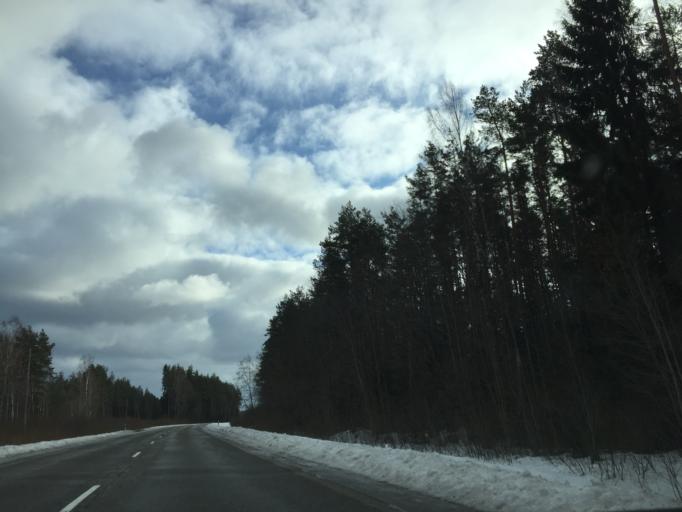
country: LV
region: Aloja
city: Staicele
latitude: 57.8585
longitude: 24.7039
